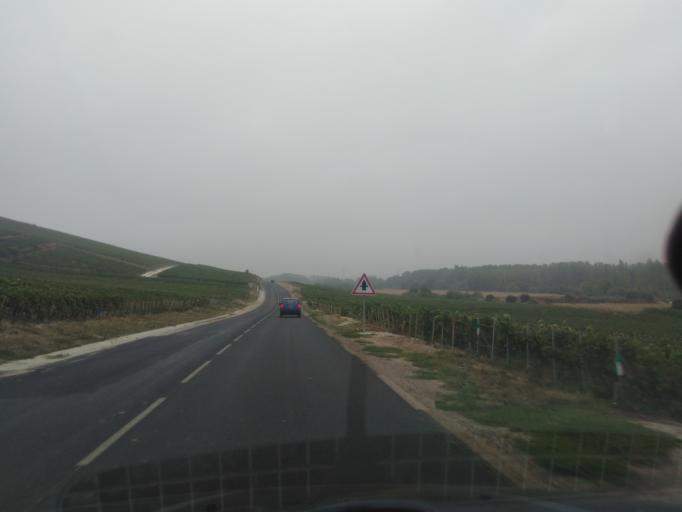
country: FR
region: Champagne-Ardenne
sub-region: Departement de la Marne
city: Damery
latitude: 49.0697
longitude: 3.9022
